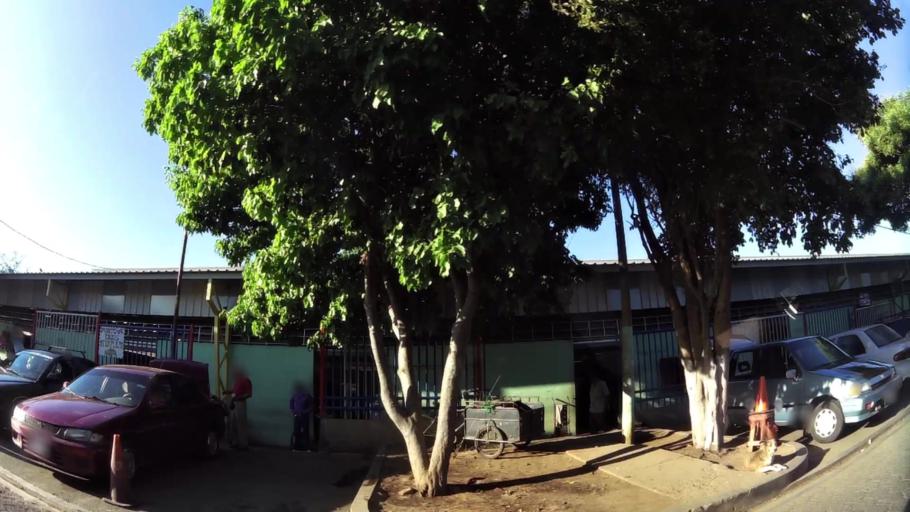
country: SV
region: Sonsonate
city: Sonsonate
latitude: 13.7163
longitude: -89.7309
